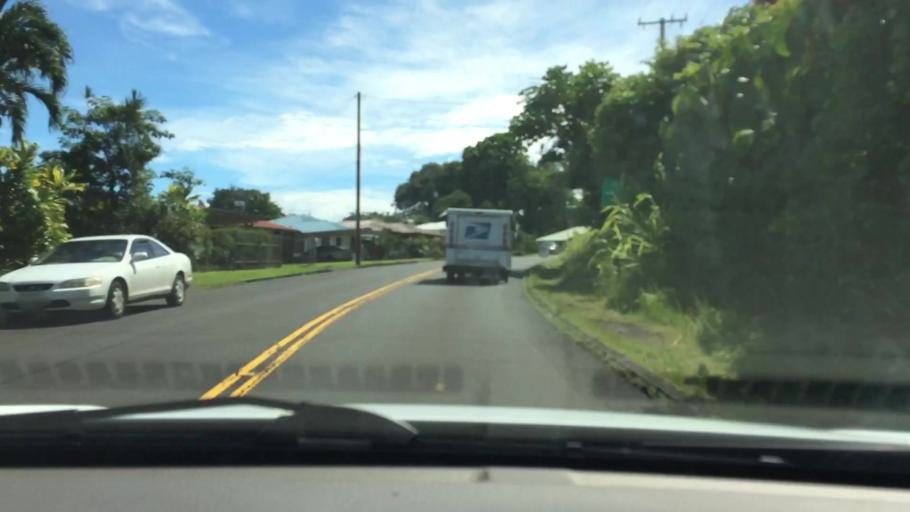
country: US
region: Hawaii
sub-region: Hawaii County
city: Hilo
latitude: 19.7252
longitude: -155.0917
